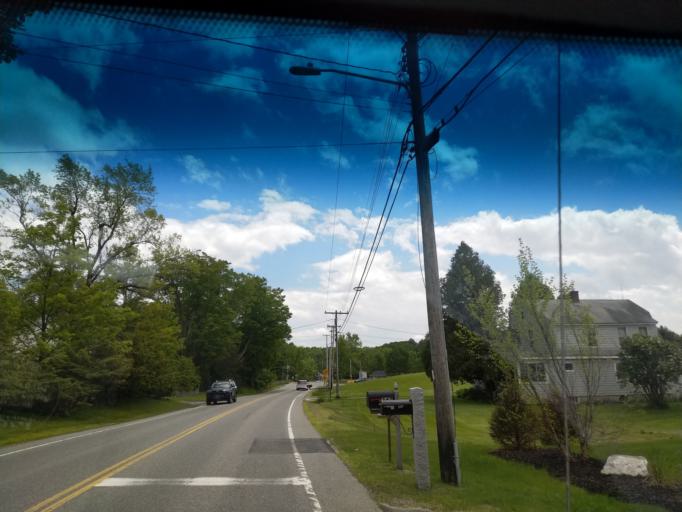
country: US
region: Maine
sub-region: Cumberland County
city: Falmouth
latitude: 43.7414
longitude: -70.2893
